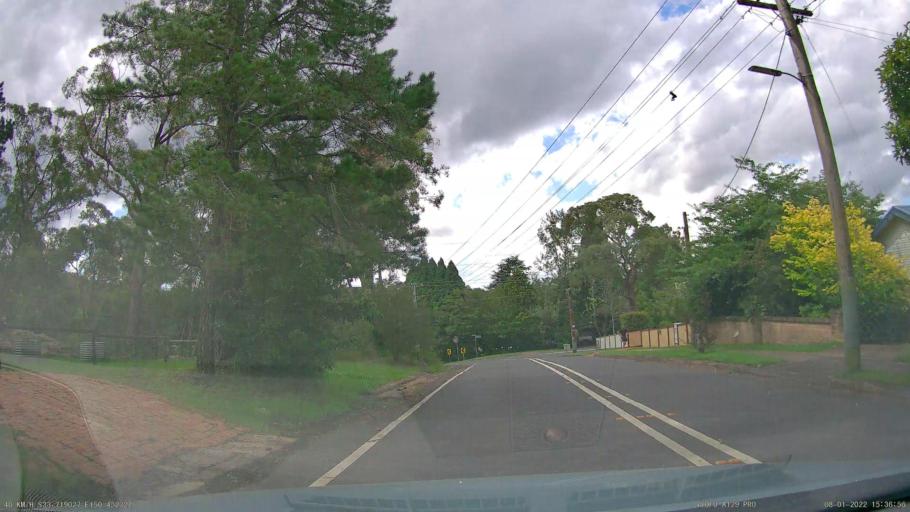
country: AU
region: New South Wales
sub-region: Blue Mountains Municipality
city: Hazelbrook
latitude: -33.7190
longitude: 150.4523
